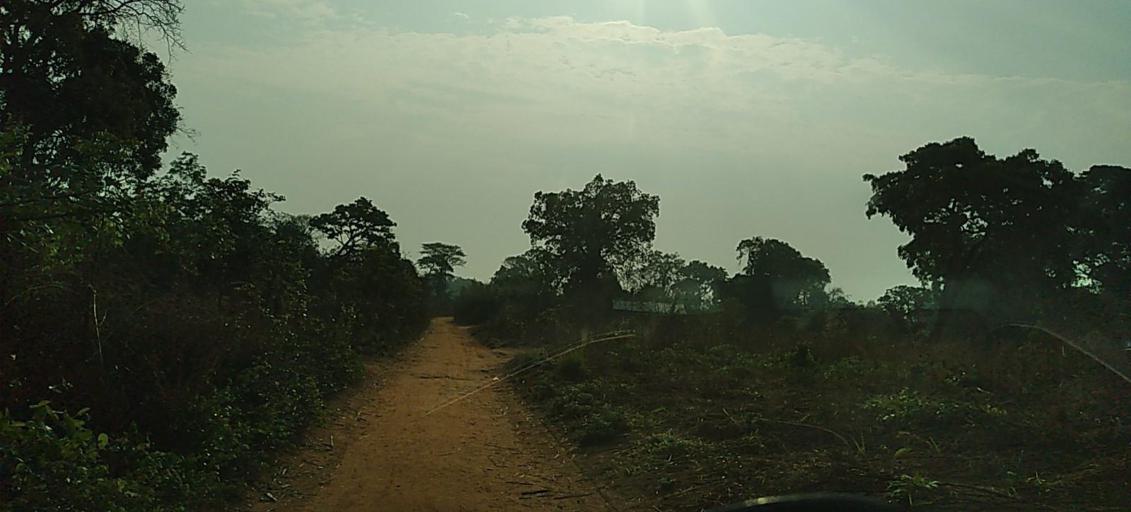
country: ZM
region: North-Western
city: Solwezi
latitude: -12.3531
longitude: 26.5352
